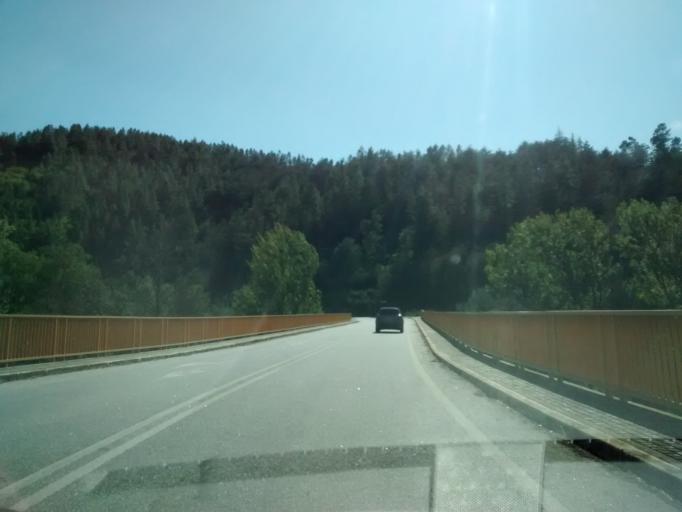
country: PT
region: Castelo Branco
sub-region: Belmonte
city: Belmonte
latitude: 40.4015
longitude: -7.3960
